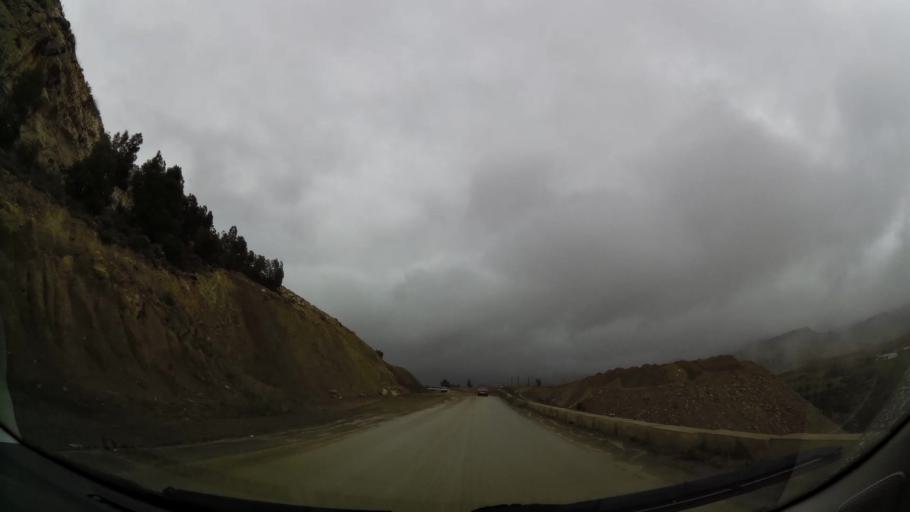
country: MA
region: Oriental
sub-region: Nador
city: Midar
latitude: 34.8972
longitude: -3.7747
